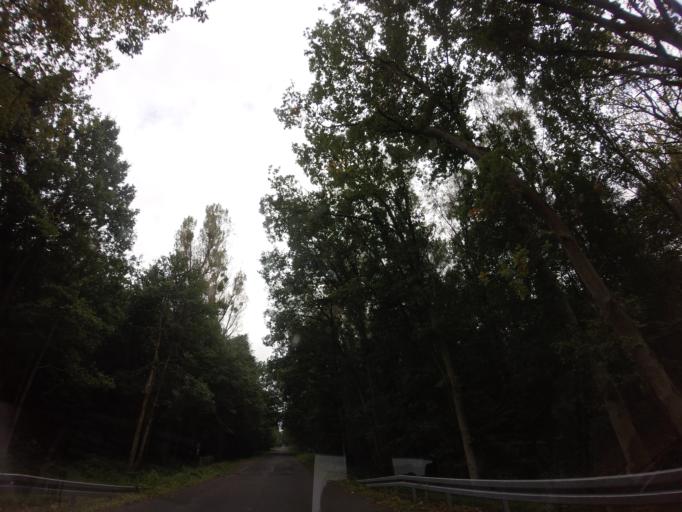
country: PL
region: West Pomeranian Voivodeship
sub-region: Powiat goleniowski
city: Stepnica
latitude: 53.6739
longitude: 14.6696
